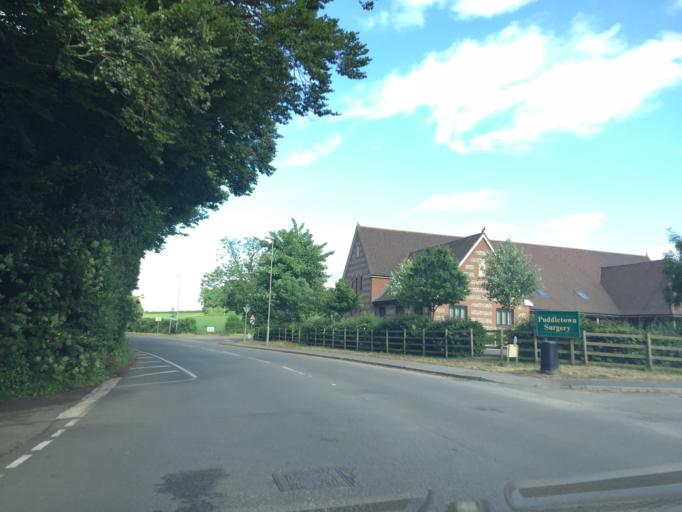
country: GB
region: England
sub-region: Dorset
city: Dorchester
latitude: 50.7466
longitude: -2.3428
